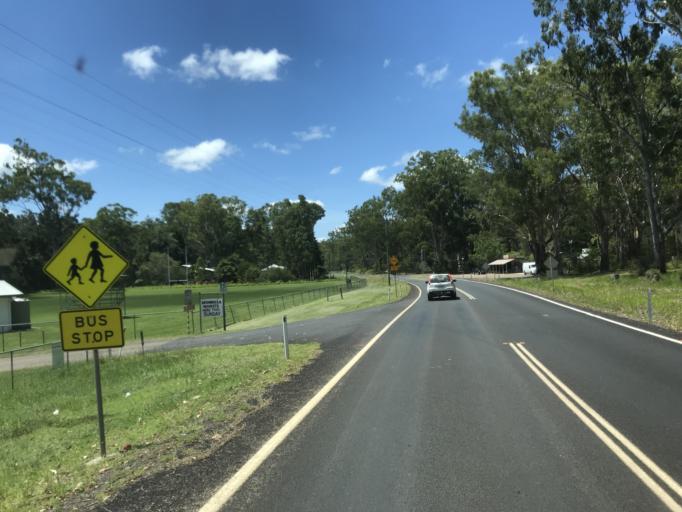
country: AU
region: Queensland
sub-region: Tablelands
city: Atherton
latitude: -17.4104
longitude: 145.3919
